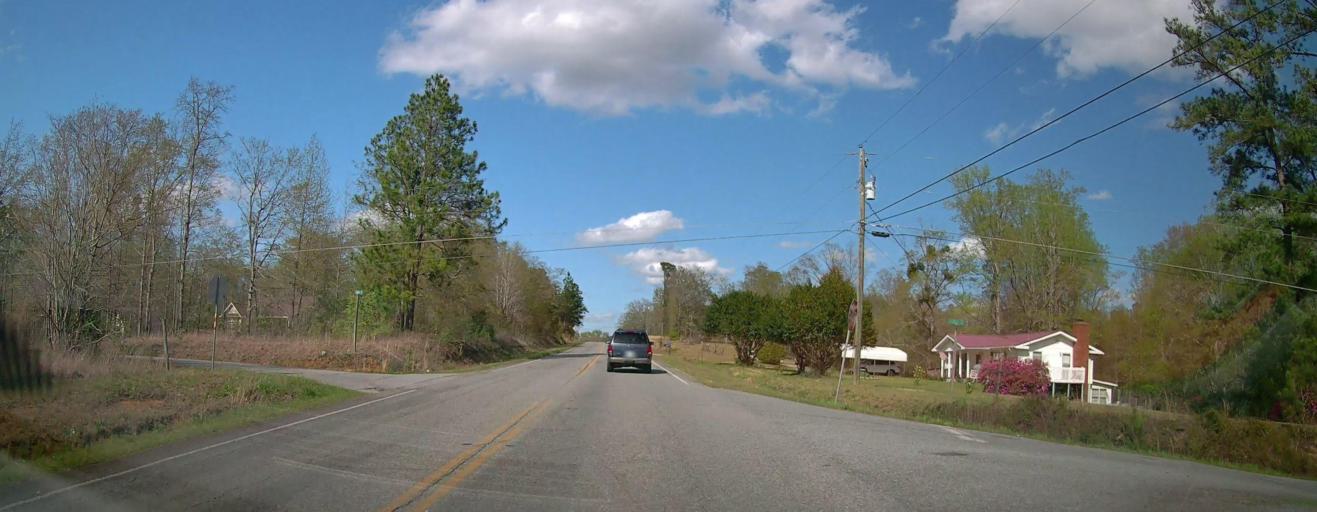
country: US
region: Georgia
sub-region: Baldwin County
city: Hardwick
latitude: 32.9978
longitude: -83.2584
